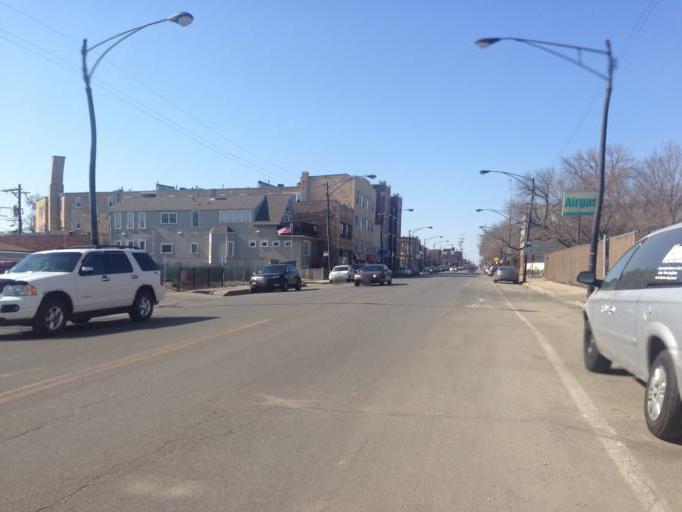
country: US
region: Illinois
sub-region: Cook County
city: Lincolnwood
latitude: 41.9398
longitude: -87.6988
